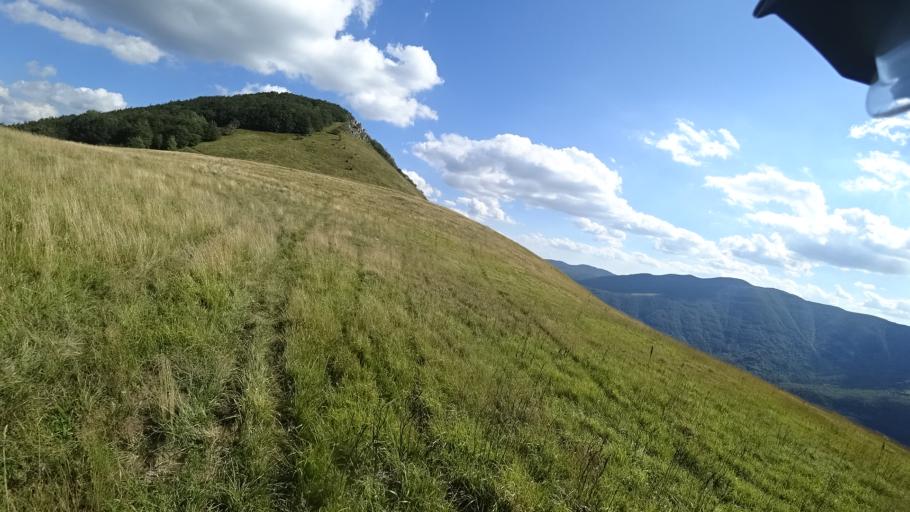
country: HR
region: Zadarska
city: Gracac
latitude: 44.3845
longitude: 16.0455
